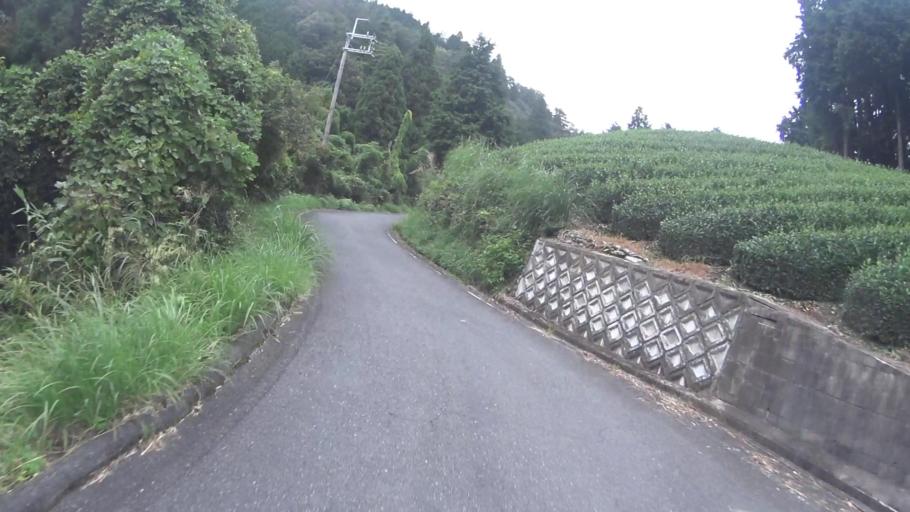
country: JP
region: Kyoto
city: Tanabe
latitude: 34.7999
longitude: 135.8793
